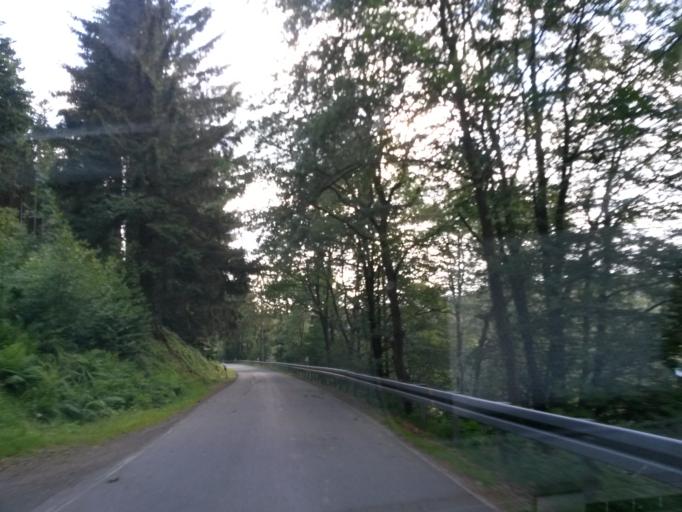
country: DE
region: North Rhine-Westphalia
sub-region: Regierungsbezirk Arnsberg
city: Herscheid
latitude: 51.1019
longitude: 7.7401
